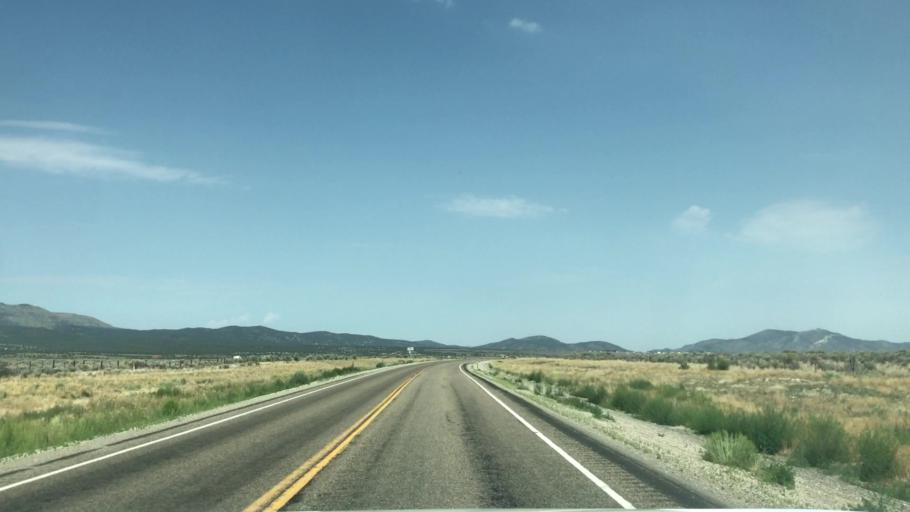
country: US
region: Nevada
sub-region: White Pine County
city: Ely
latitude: 39.1671
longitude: -114.8154
